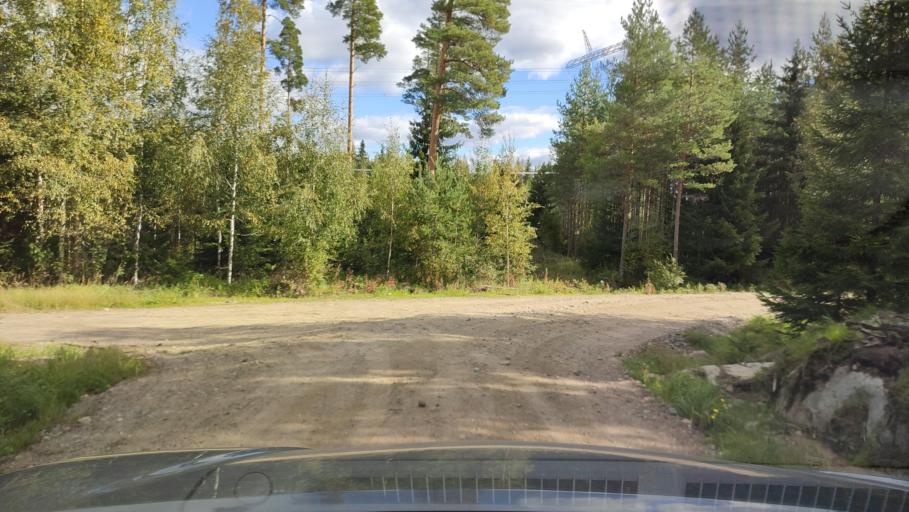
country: FI
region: Southern Ostrobothnia
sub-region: Suupohja
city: Karijoki
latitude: 62.2159
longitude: 21.6270
